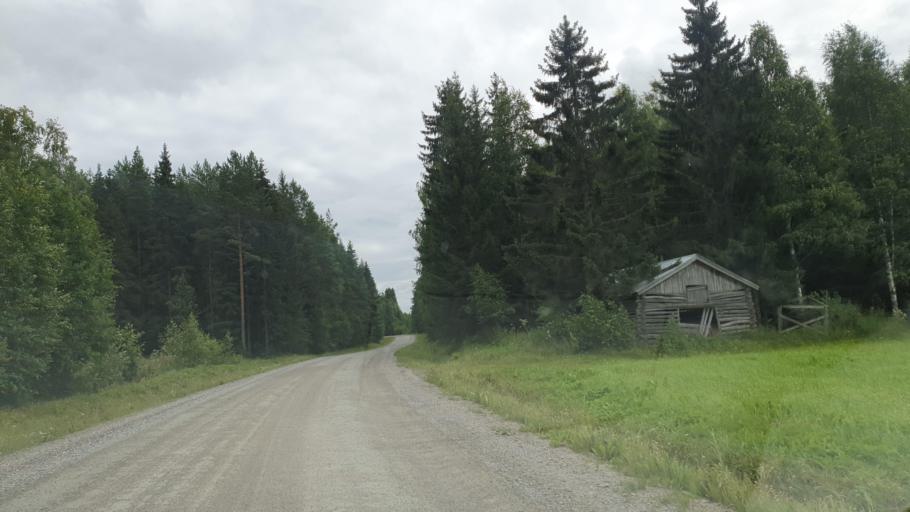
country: FI
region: Northern Savo
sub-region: Ylae-Savo
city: Iisalmi
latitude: 63.5406
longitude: 27.0722
